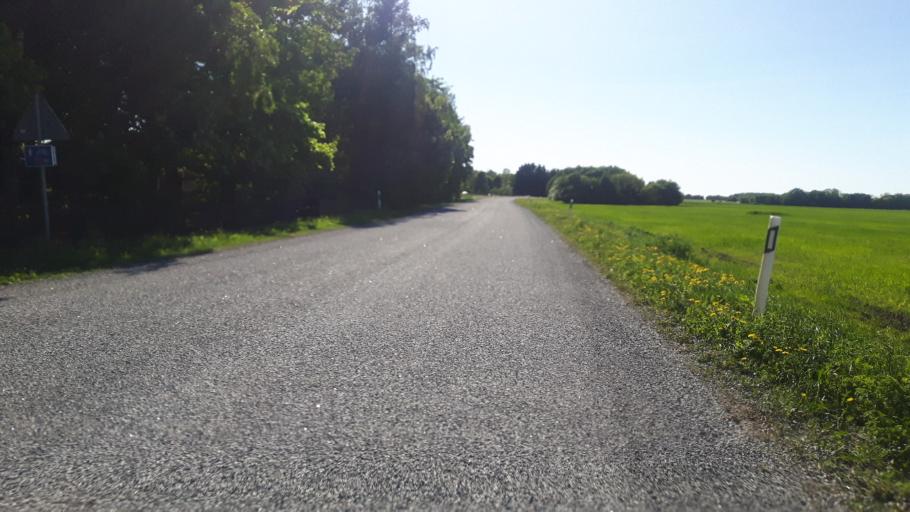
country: EE
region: Ida-Virumaa
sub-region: Kohtla-Jaerve linn
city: Kohtla-Jarve
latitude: 59.4387
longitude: 27.2837
